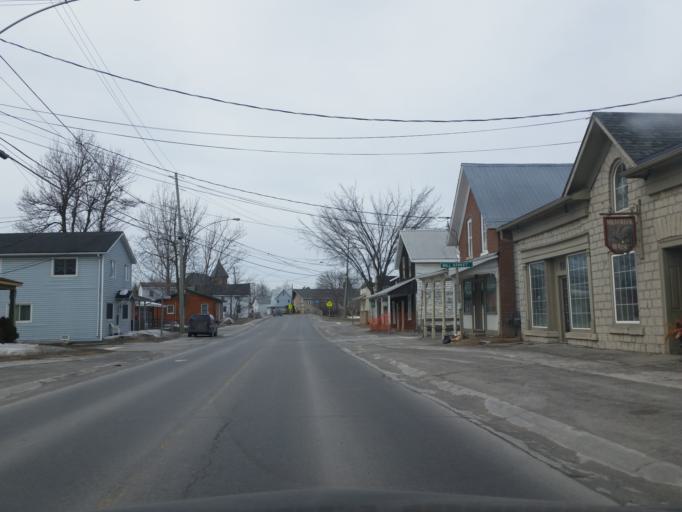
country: CA
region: Ontario
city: Skatepark
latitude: 44.2770
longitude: -76.7203
